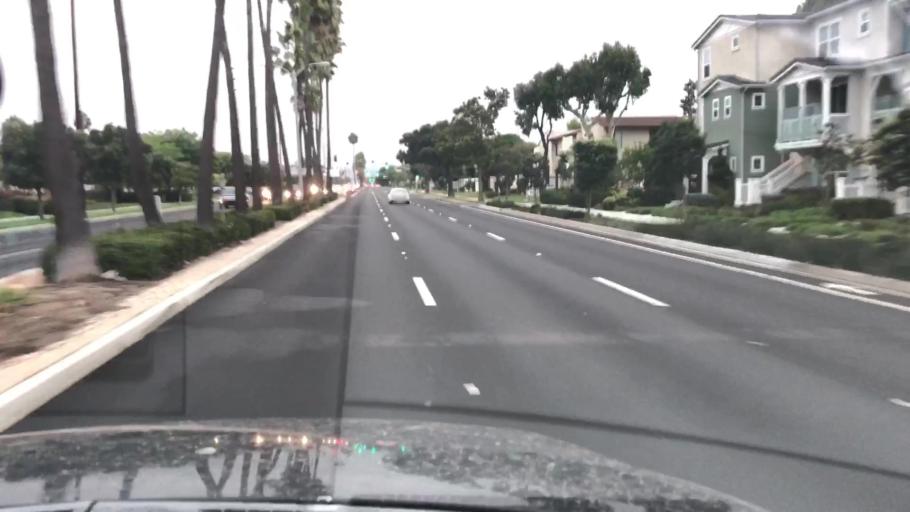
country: US
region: California
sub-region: Ventura County
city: Oxnard Shores
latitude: 34.1822
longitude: -119.2213
